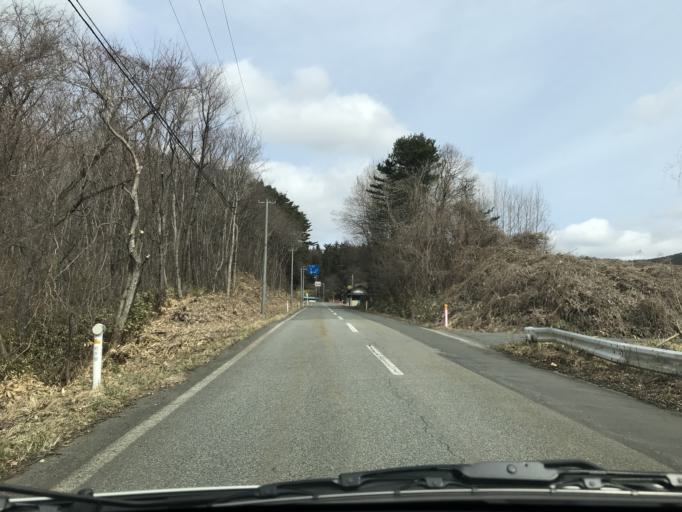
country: JP
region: Iwate
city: Kitakami
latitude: 39.2559
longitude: 141.3168
